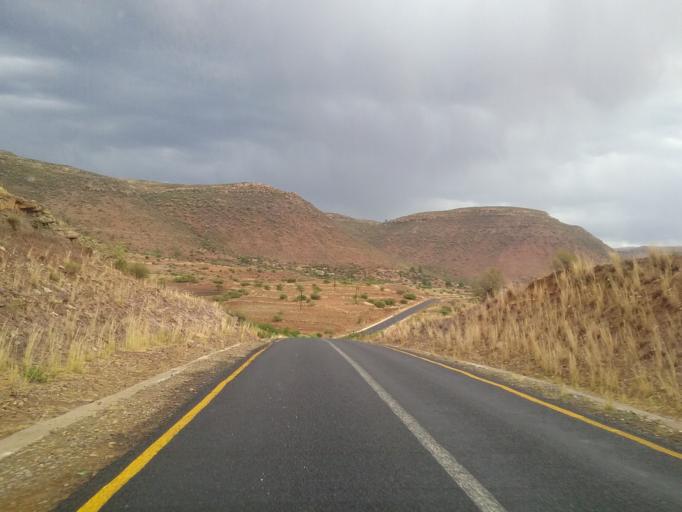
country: LS
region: Quthing
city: Quthing
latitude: -30.3473
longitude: 27.7214
